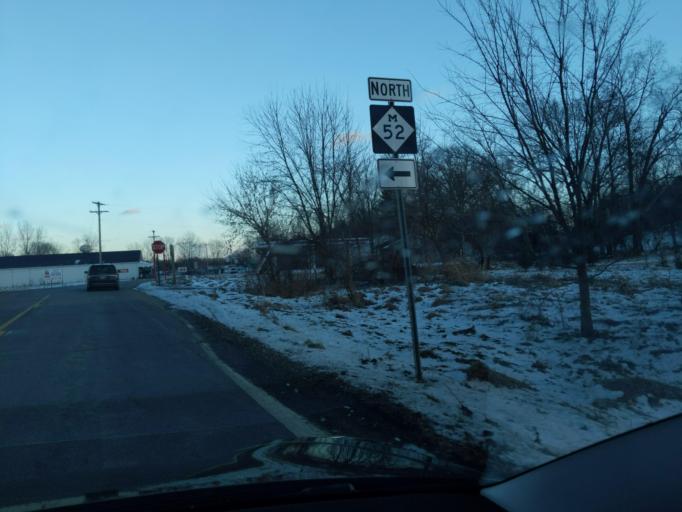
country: US
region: Michigan
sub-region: Ingham County
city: Stockbridge
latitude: 42.4539
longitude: -84.1906
